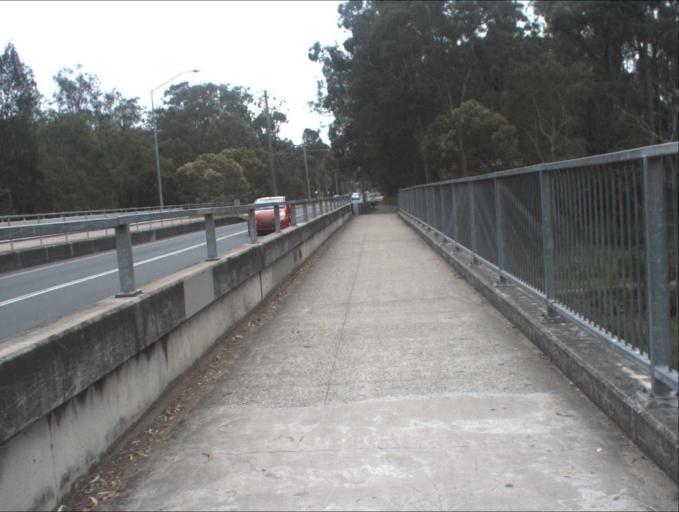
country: AU
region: Queensland
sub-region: Logan
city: Park Ridge South
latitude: -27.6717
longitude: 153.0529
